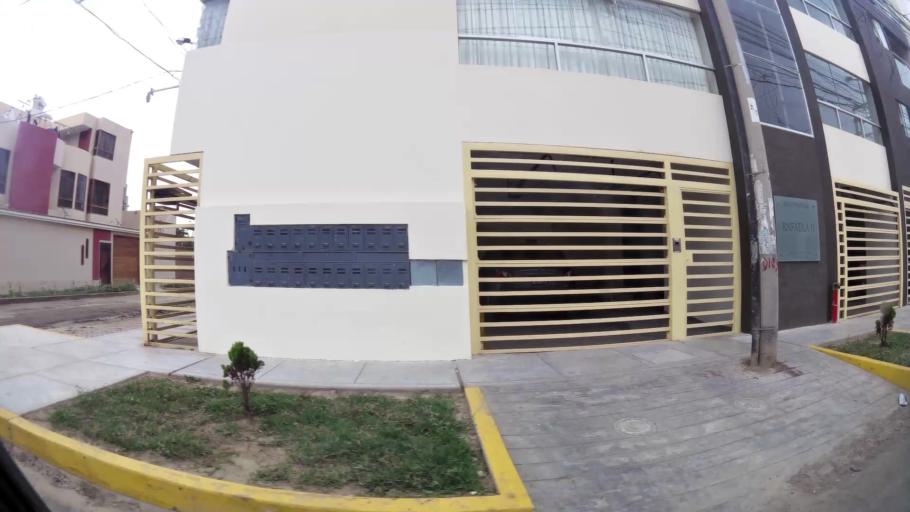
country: PE
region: La Libertad
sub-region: Provincia de Trujillo
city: Trujillo
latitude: -8.1197
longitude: -79.0446
